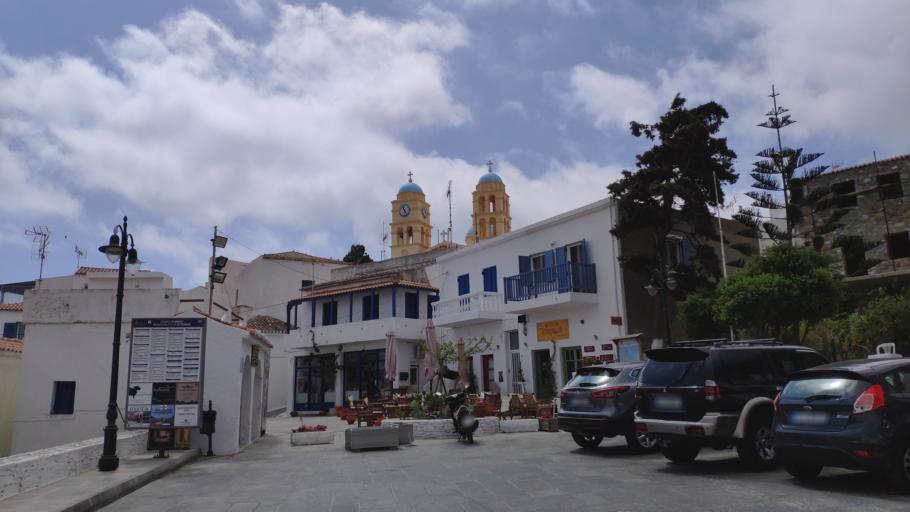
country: GR
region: South Aegean
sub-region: Nomos Kykladon
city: Kythnos
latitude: 37.3834
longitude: 24.4304
